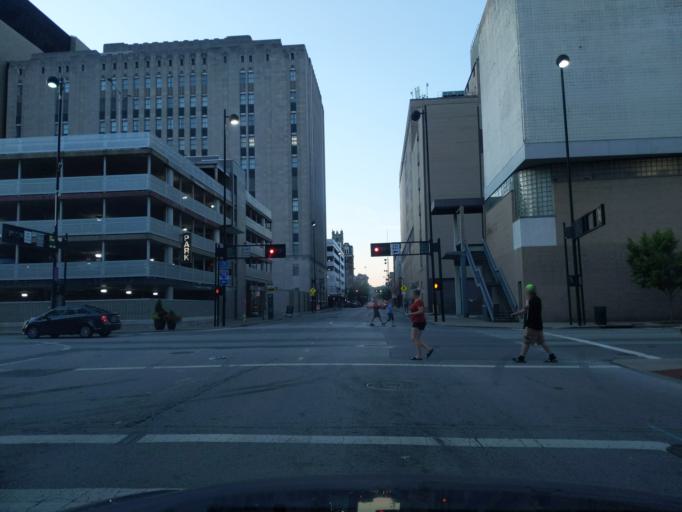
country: US
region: Kentucky
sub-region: Kenton County
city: Covington
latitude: 39.1019
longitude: -84.5164
